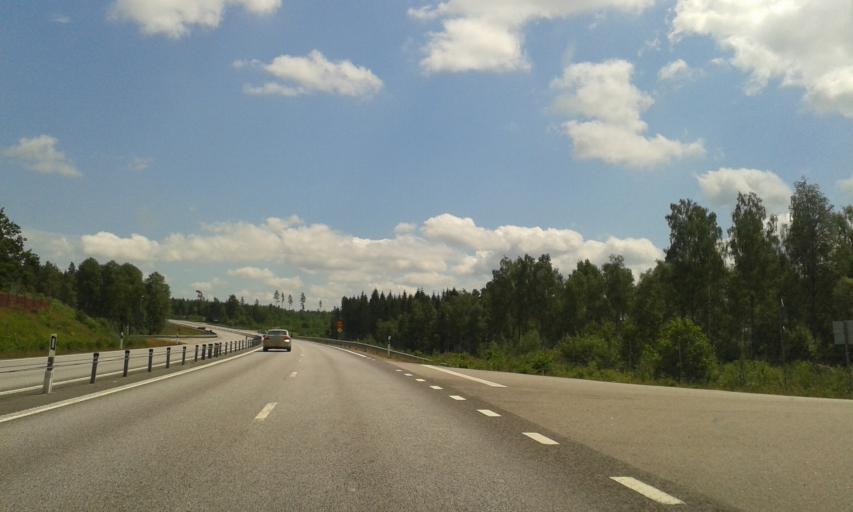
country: SE
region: Kronoberg
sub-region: Vaxjo Kommun
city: Gemla
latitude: 56.8981
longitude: 14.6805
